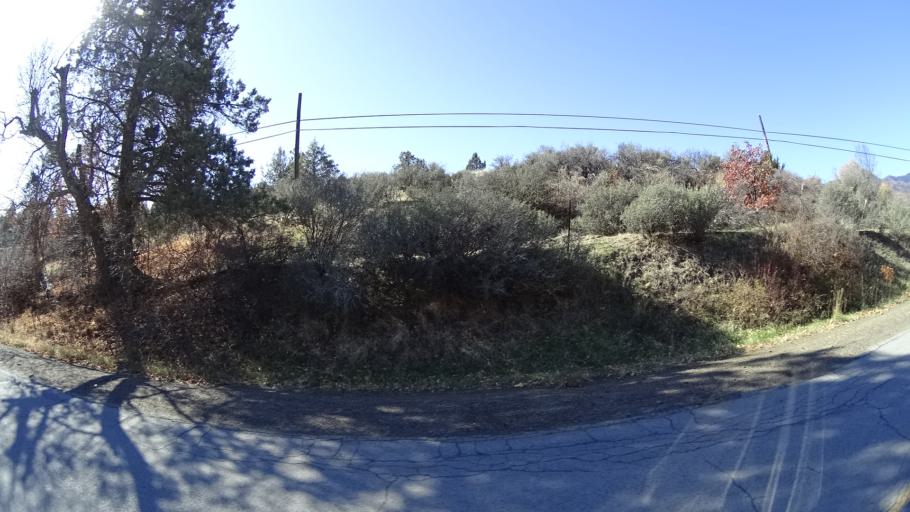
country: US
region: California
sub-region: Siskiyou County
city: Montague
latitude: 41.9184
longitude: -122.5667
